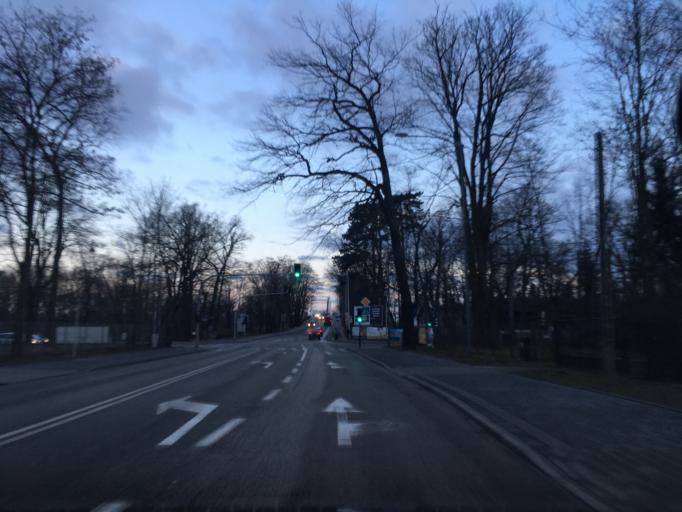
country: PL
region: Masovian Voivodeship
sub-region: Powiat grodziski
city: Grodzisk Mazowiecki
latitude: 52.1094
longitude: 20.6309
